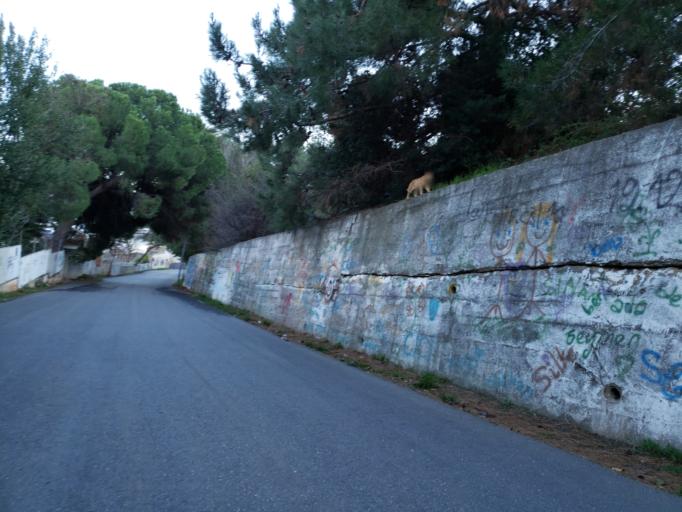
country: TR
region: Istanbul
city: Adalan
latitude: 40.8824
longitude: 29.0989
